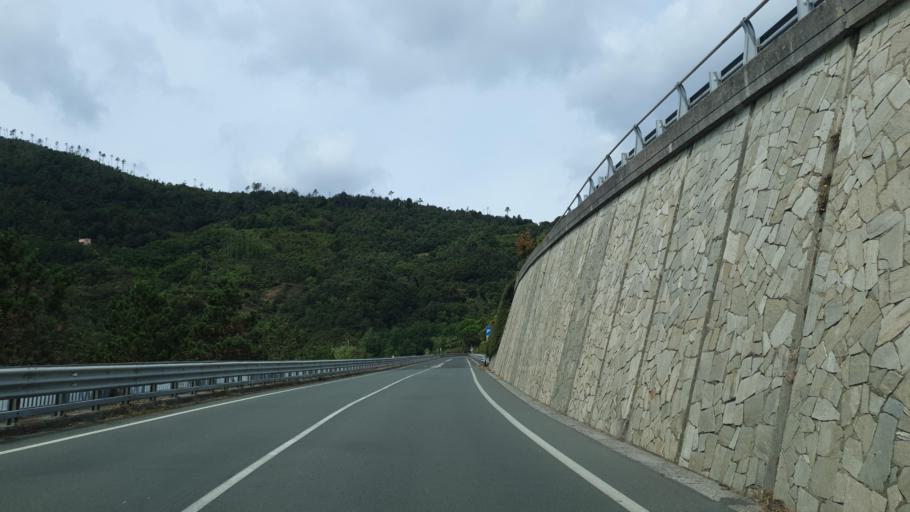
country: IT
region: Liguria
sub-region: Provincia di La Spezia
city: Levanto
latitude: 44.1987
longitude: 9.6253
